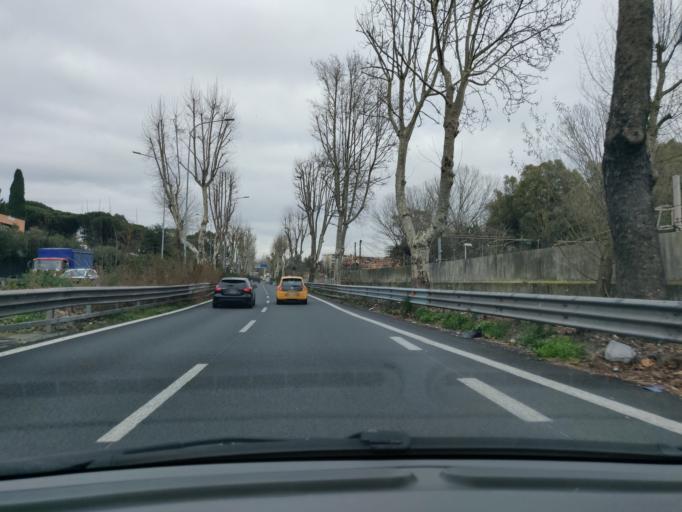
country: IT
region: Latium
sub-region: Citta metropolitana di Roma Capitale
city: La Massimina-Casal Lumbroso
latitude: 41.8844
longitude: 12.3972
